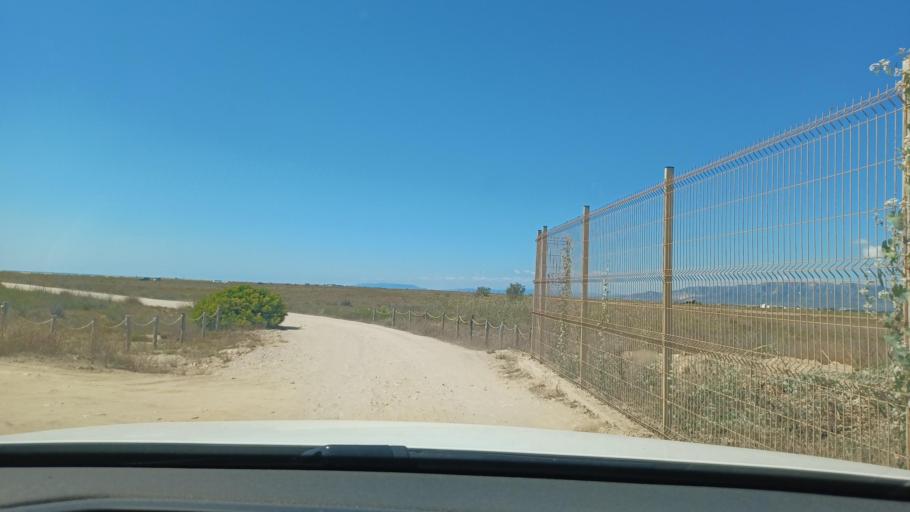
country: ES
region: Catalonia
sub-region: Provincia de Tarragona
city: Deltebre
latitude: 40.6482
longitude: 0.7639
